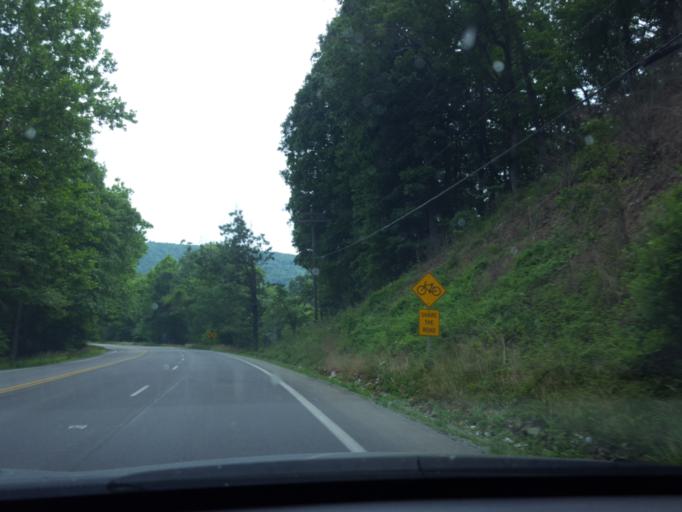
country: US
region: Virginia
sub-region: City of Waynesboro
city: Waynesboro
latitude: 38.0475
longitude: -78.8671
